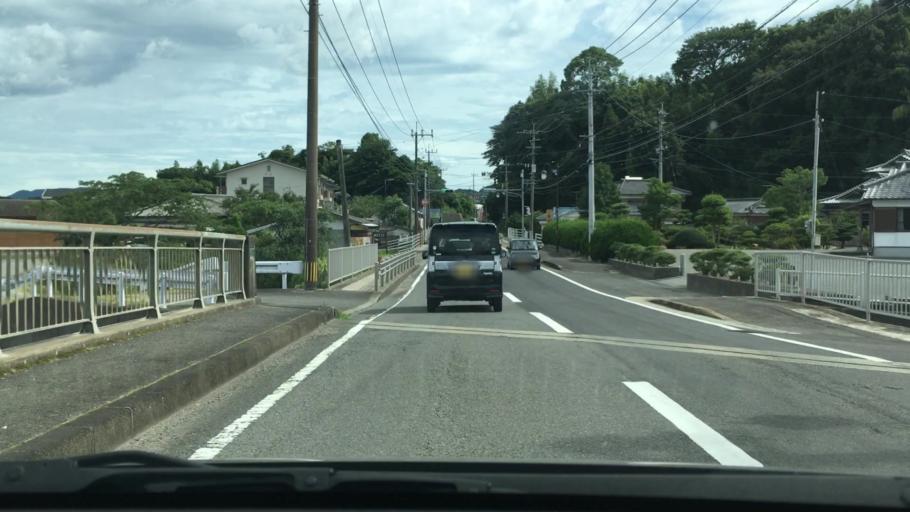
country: JP
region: Nagasaki
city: Togitsu
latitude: 32.9128
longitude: 129.7844
